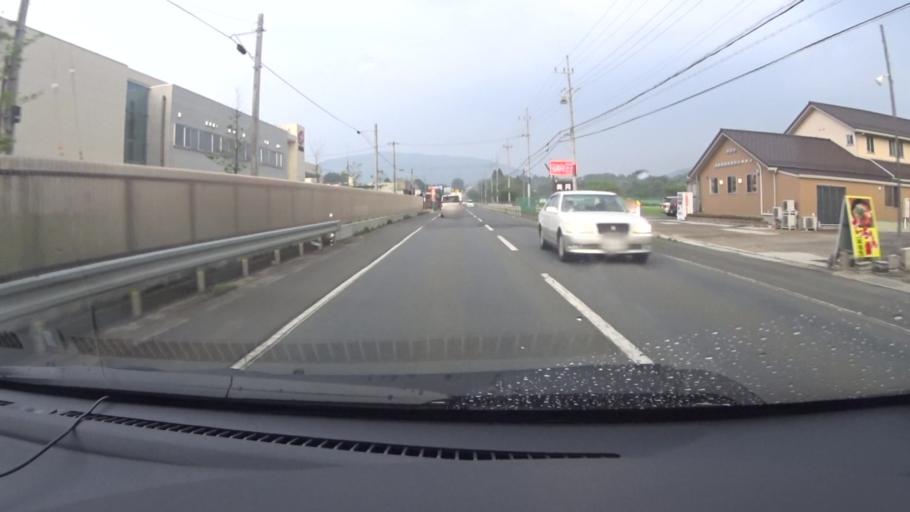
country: JP
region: Kyoto
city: Ayabe
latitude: 35.1792
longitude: 135.4212
